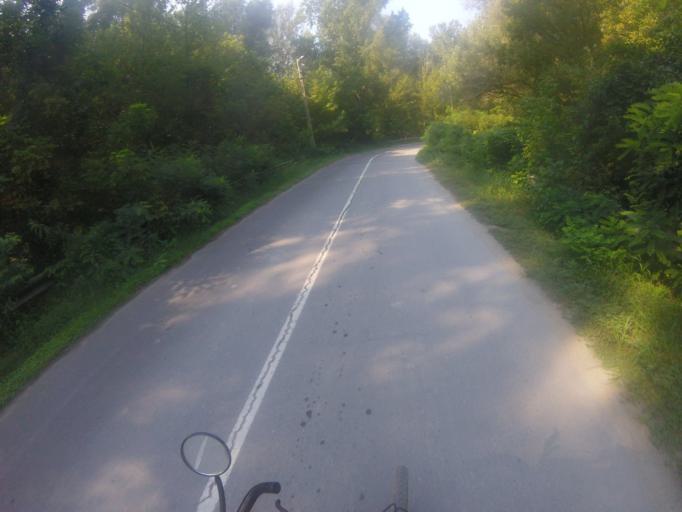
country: HU
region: Bacs-Kiskun
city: Baja
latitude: 46.1924
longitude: 18.9198
